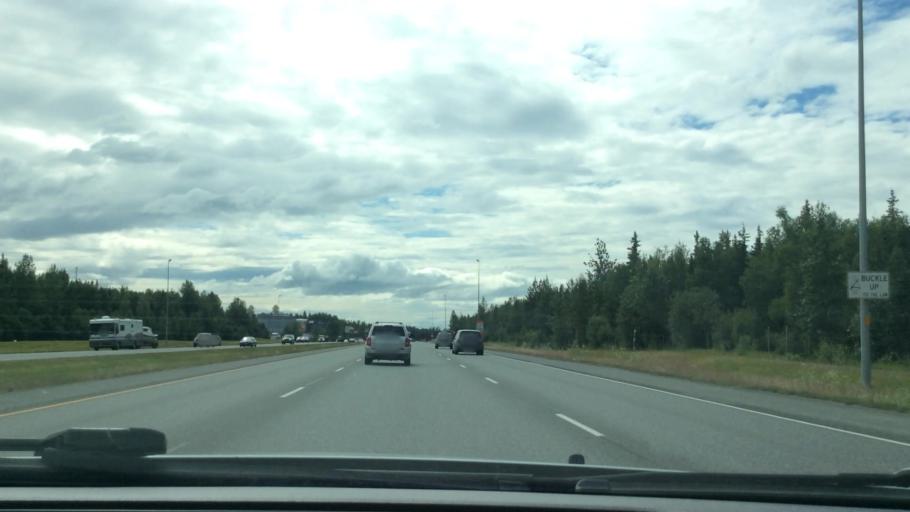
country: US
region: Alaska
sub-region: Anchorage Municipality
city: Elmendorf Air Force Base
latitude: 61.2351
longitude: -149.7035
